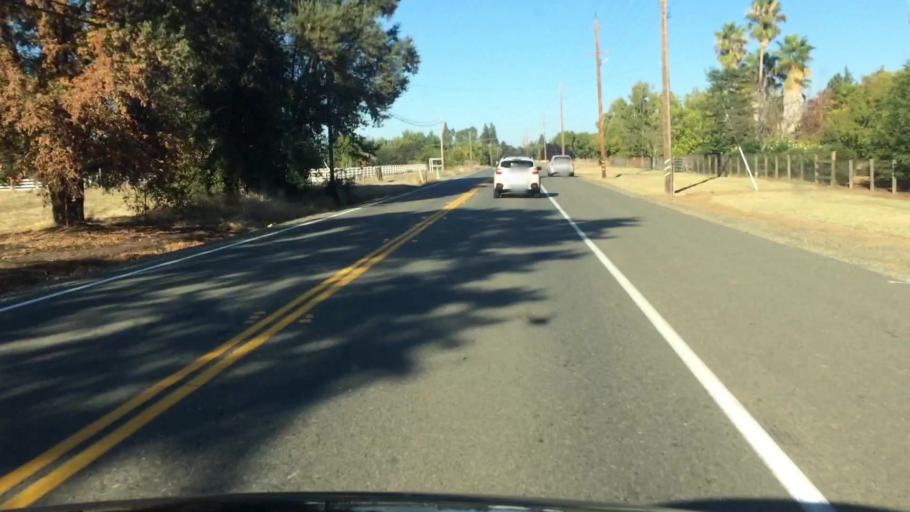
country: US
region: California
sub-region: Sacramento County
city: Wilton
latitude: 38.4344
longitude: -121.1985
